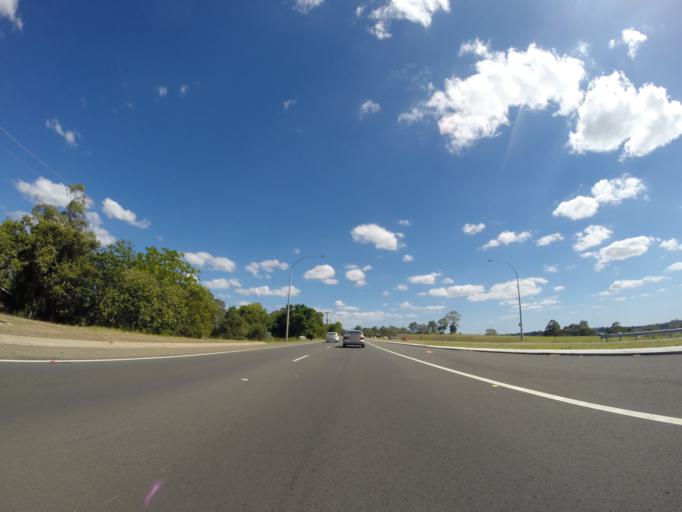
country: AU
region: New South Wales
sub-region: Campbelltown Municipality
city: Campbelltown
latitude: -34.0811
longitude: 150.8081
